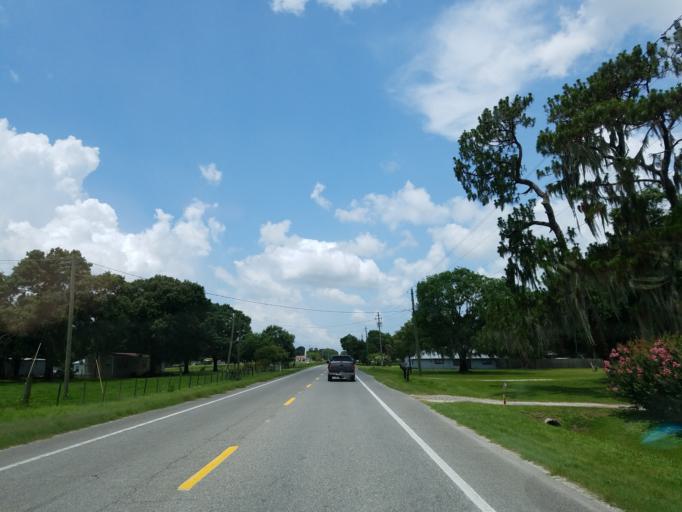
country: US
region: Florida
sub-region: Polk County
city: Willow Oak
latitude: 27.8506
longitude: -82.0822
